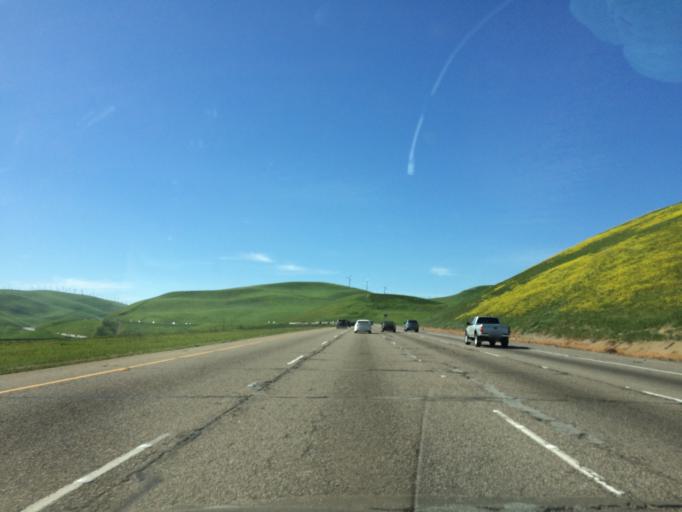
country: US
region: California
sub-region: San Joaquin County
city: Mountain House
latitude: 37.7353
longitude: -121.6243
